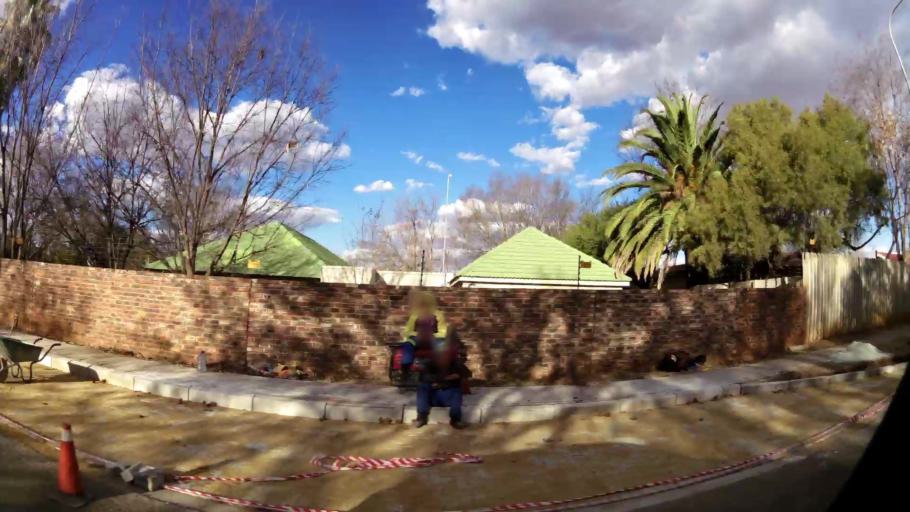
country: ZA
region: North-West
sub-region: Dr Kenneth Kaunda District Municipality
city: Potchefstroom
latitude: -26.6896
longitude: 27.0985
